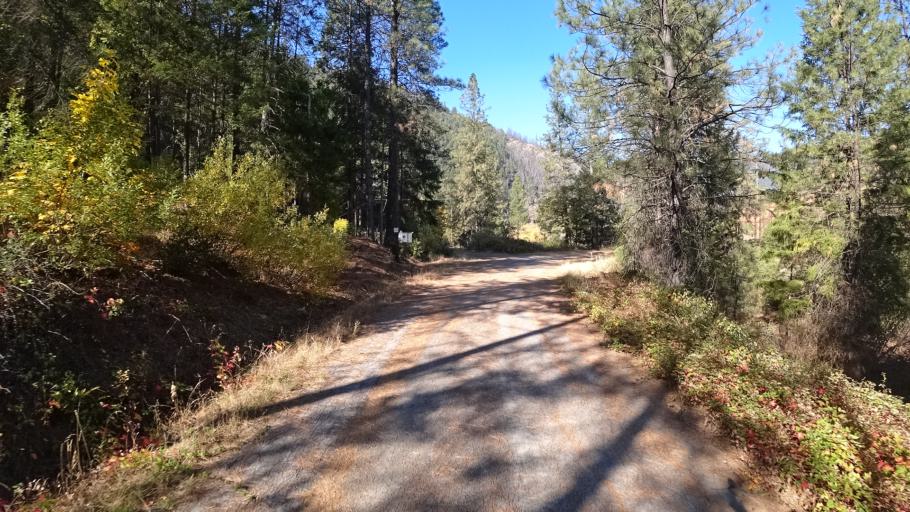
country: US
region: California
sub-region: Siskiyou County
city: Happy Camp
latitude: 41.7743
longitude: -123.0342
